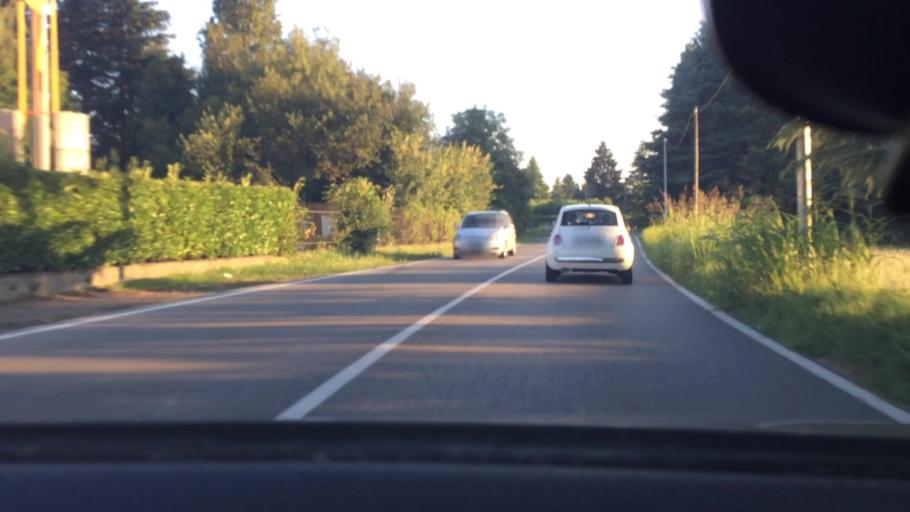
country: IT
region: Lombardy
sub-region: Provincia di Como
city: Fino Mornasco
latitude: 45.7379
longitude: 9.0445
